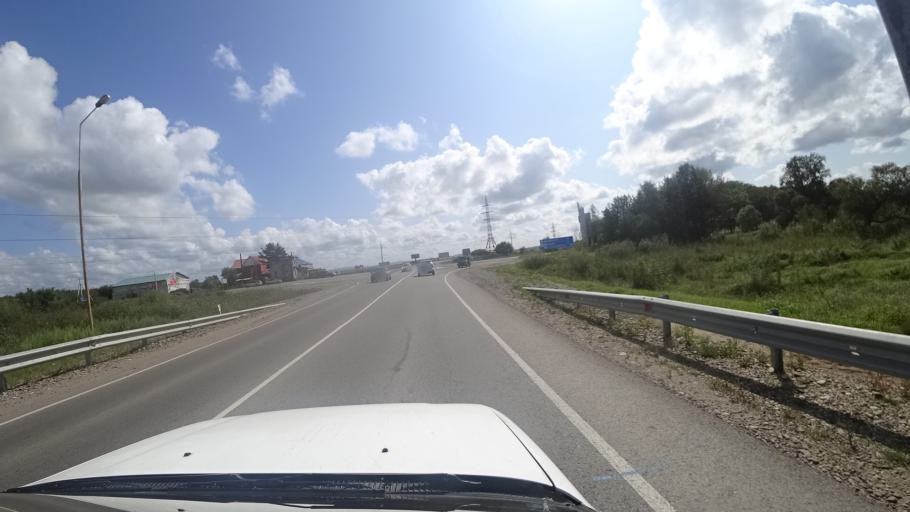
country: RU
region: Primorskiy
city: Dal'nerechensk
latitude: 45.9185
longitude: 133.7723
